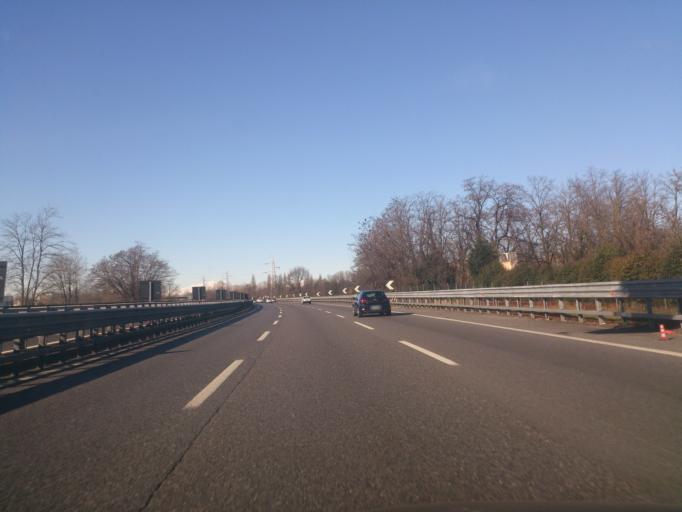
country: IT
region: Lombardy
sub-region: Citta metropolitana di Milano
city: Buccinasco
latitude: 45.4096
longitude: 9.1084
